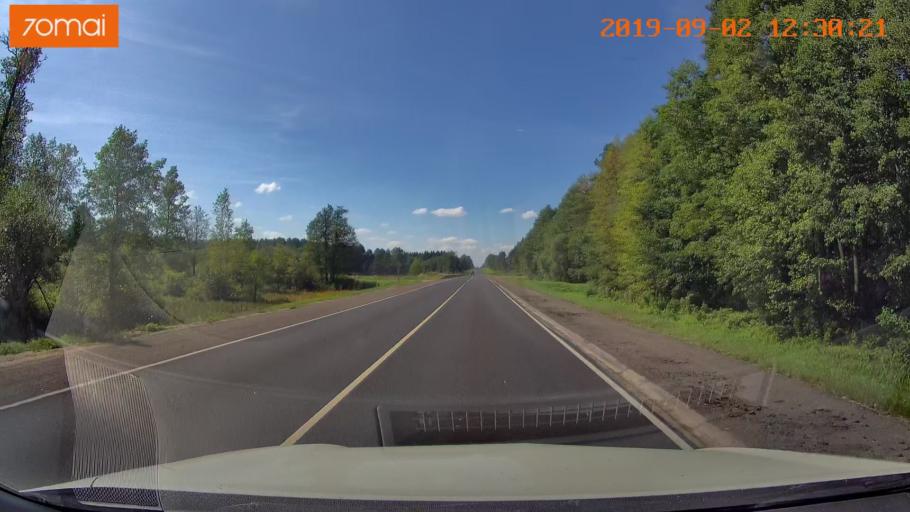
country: RU
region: Smolensk
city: Shumyachi
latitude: 53.8328
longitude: 32.4767
